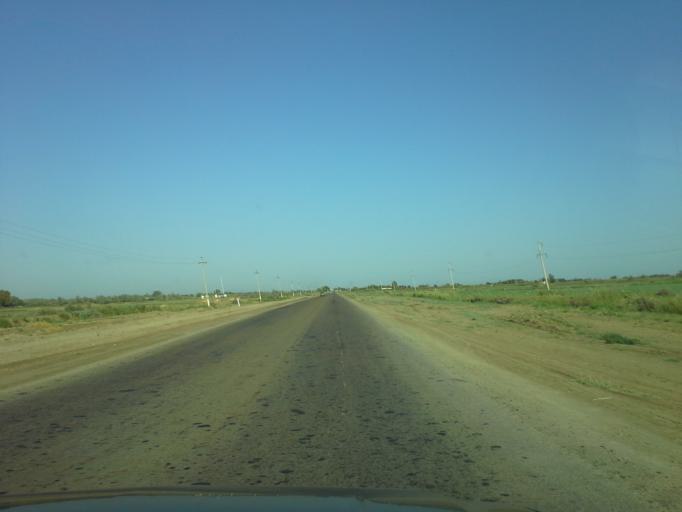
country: UZ
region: Karakalpakstan
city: Khujayli
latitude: 42.2244
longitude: 59.4804
